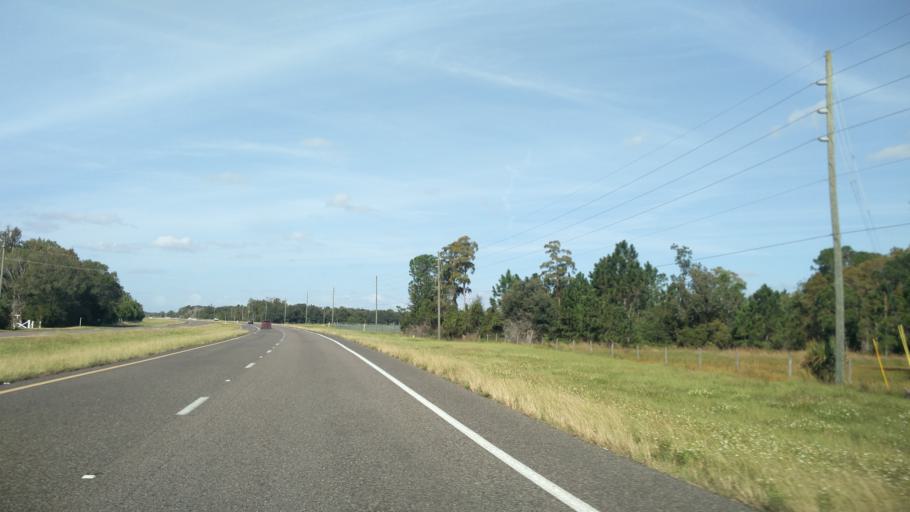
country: US
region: Florida
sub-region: Brevard County
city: June Park
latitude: 28.1154
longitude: -80.9259
